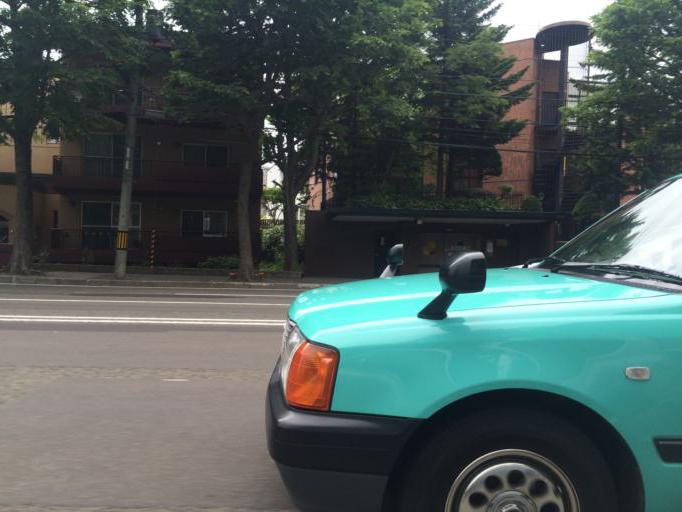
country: JP
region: Hokkaido
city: Sapporo
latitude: 43.0563
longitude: 141.3081
